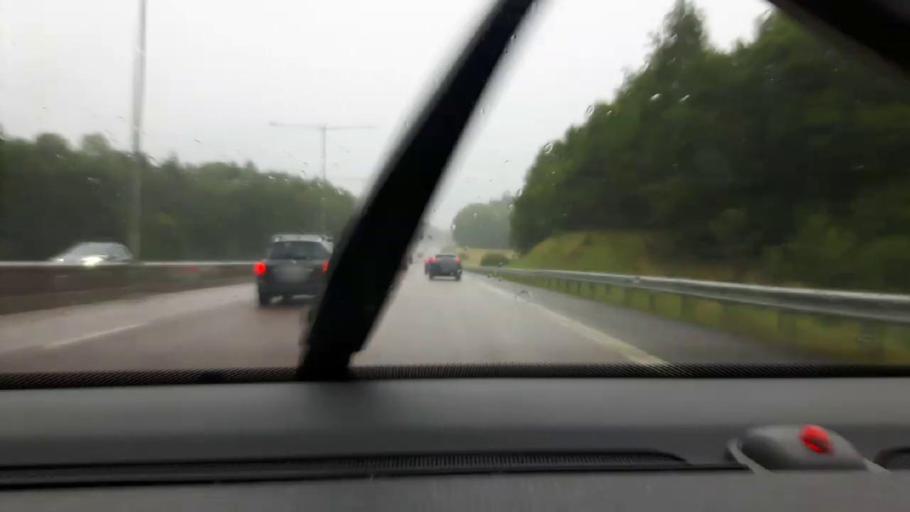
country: SE
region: Stockholm
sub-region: Salems Kommun
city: Ronninge
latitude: 59.2109
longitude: 17.7390
